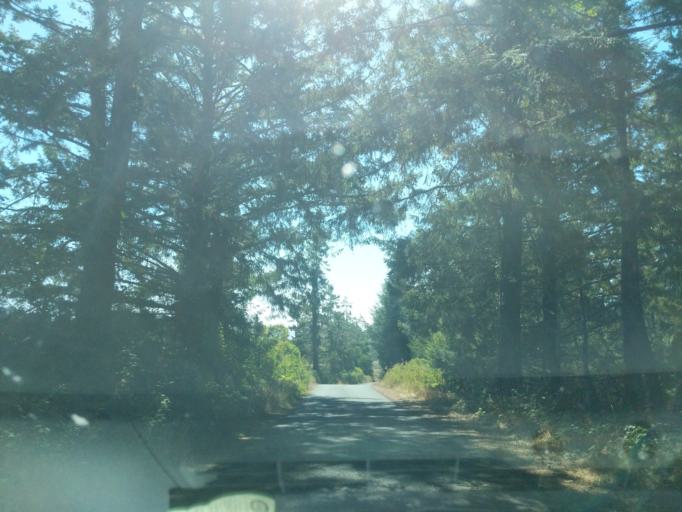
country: US
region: California
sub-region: Sonoma County
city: Monte Rio
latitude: 38.5218
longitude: -123.2433
